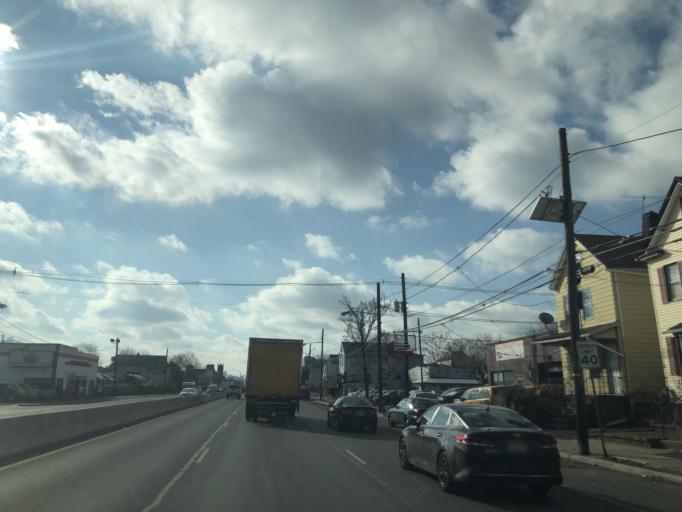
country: US
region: New Jersey
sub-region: Union County
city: Elizabeth
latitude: 40.6726
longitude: -74.2007
